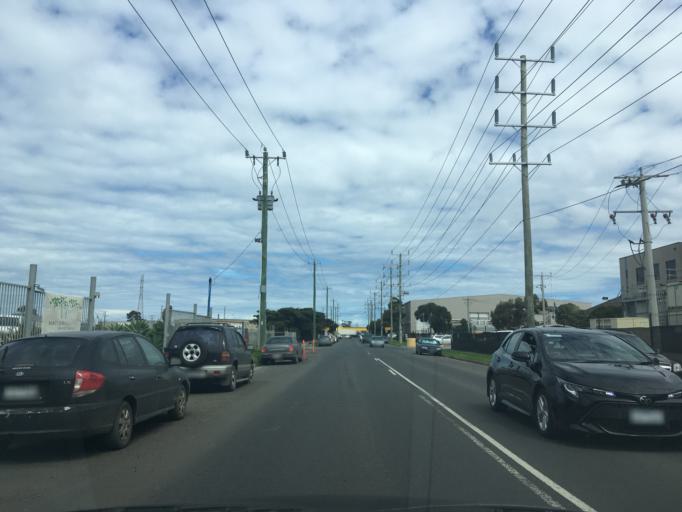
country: AU
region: Victoria
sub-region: Brimbank
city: Sunshine West
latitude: -37.8260
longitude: 144.7967
